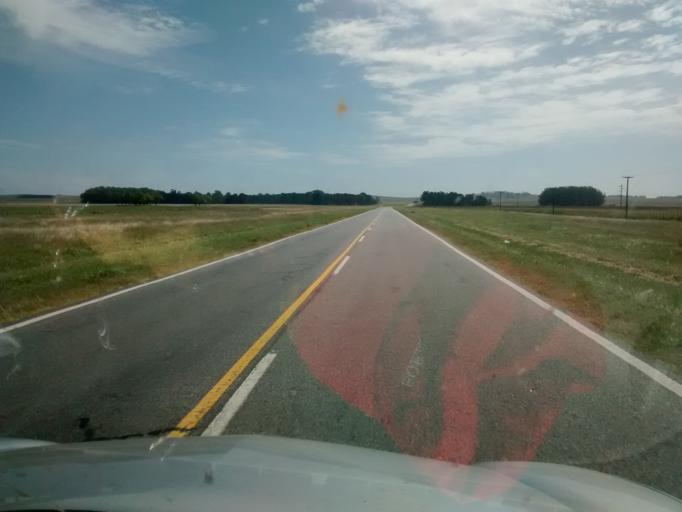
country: AR
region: Buenos Aires
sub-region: Partido de Balcarce
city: Balcarce
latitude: -37.6576
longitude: -58.5593
